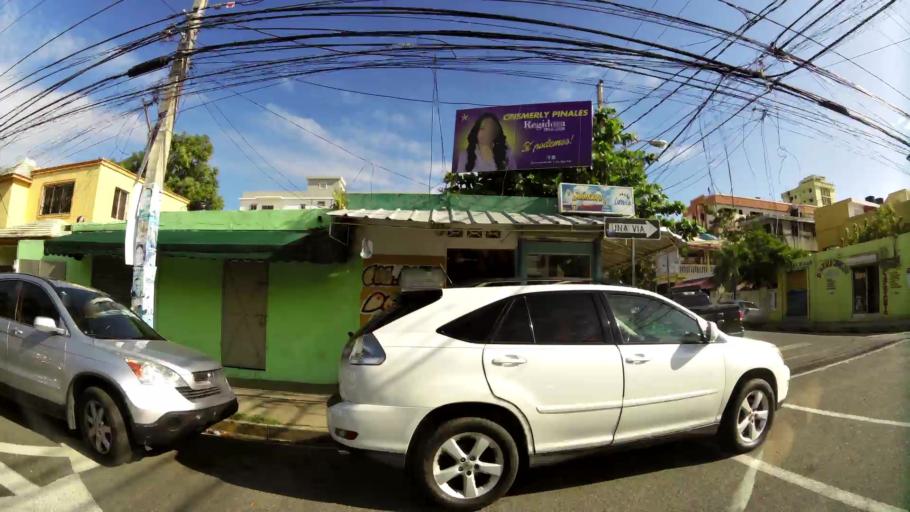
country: DO
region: Santo Domingo
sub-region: Santo Domingo
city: Santo Domingo Este
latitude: 18.4889
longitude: -69.8755
